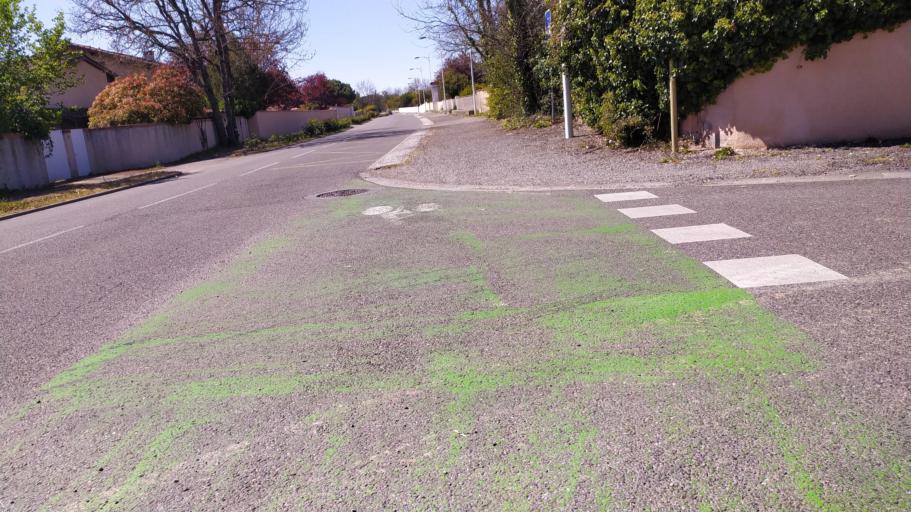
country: FR
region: Midi-Pyrenees
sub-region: Departement de la Haute-Garonne
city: Tournefeuille
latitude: 43.5869
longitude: 1.3146
